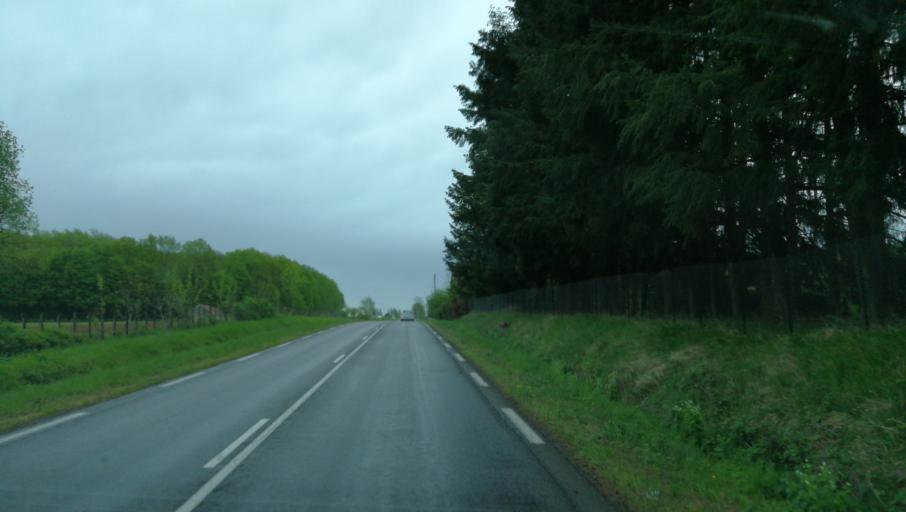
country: FR
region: Franche-Comte
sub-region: Departement du Jura
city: Montmorot
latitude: 46.6935
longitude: 5.4960
